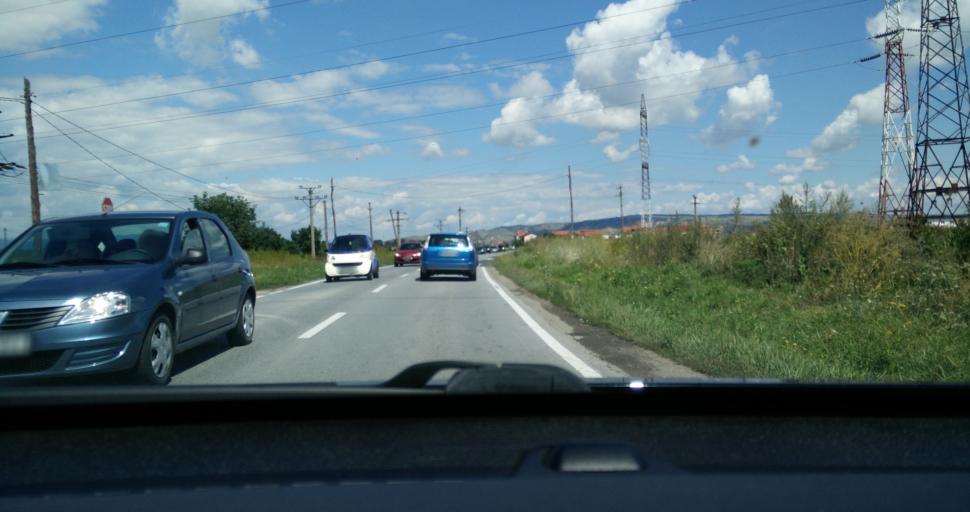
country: RO
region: Alba
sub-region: Municipiul Sebes
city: Petresti
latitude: 45.9308
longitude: 23.5604
